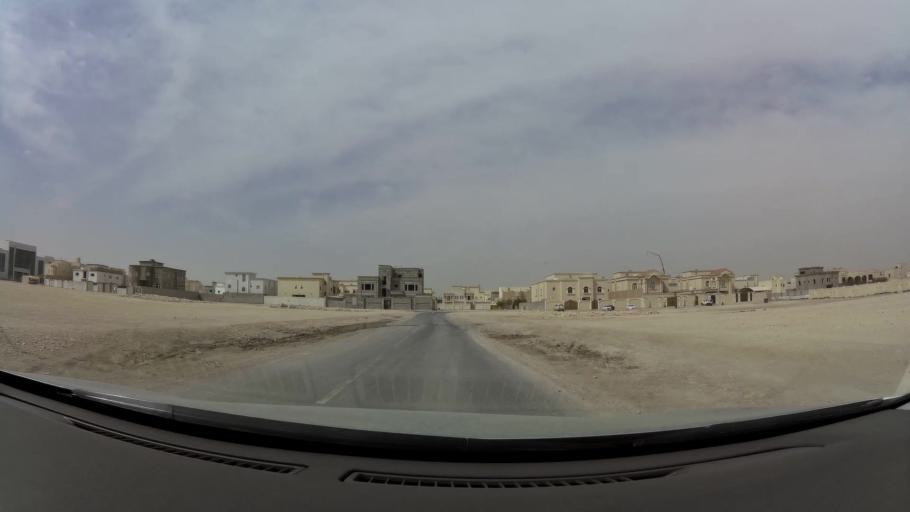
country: QA
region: Al Wakrah
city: Al Wukayr
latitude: 25.2013
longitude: 51.4669
